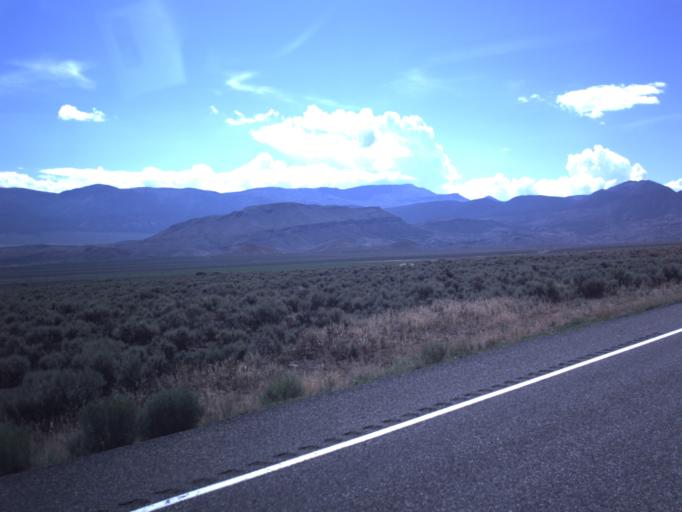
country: US
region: Utah
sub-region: Piute County
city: Junction
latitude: 38.3615
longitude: -112.2230
